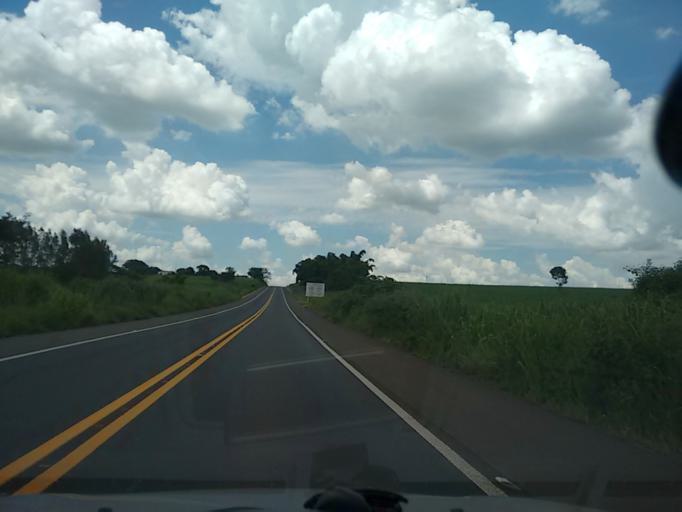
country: BR
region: Sao Paulo
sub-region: Osvaldo Cruz
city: Osvaldo Cruz
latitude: -21.8476
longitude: -50.8341
